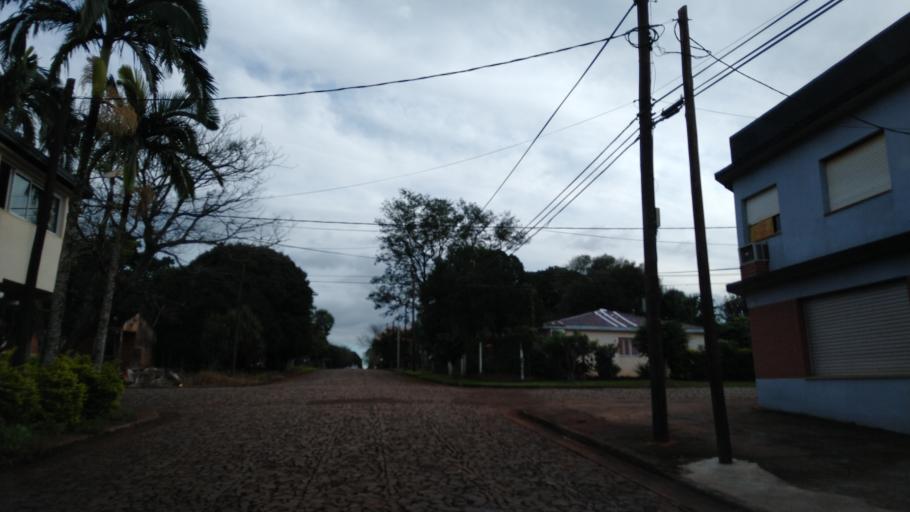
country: AR
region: Misiones
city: Jardin America
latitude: -27.0436
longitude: -55.2397
